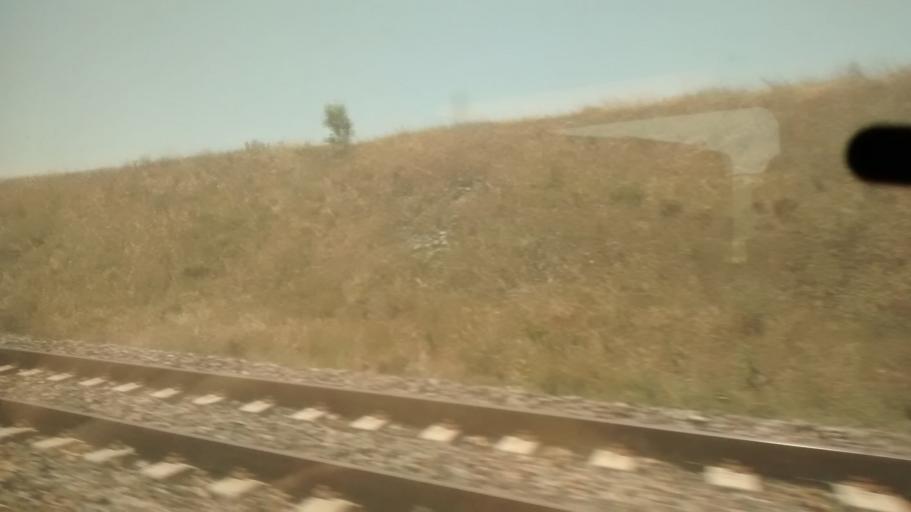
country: FR
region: Languedoc-Roussillon
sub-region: Departement du Gard
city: Les Angles
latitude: 43.9731
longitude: 4.7370
